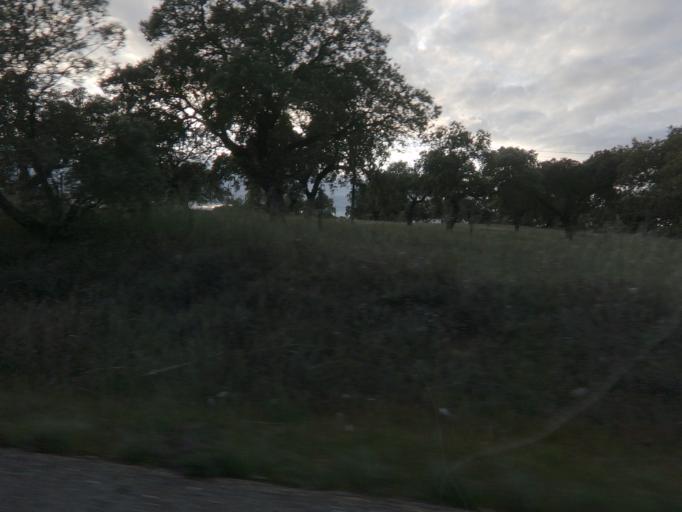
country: ES
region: Extremadura
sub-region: Provincia de Badajoz
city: Puebla de Obando
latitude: 39.1404
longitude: -6.6550
